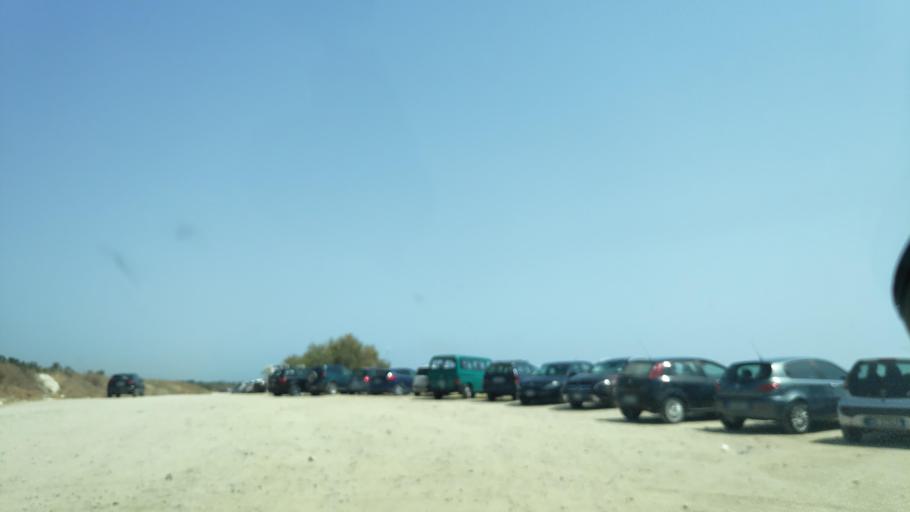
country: IT
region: Calabria
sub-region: Provincia di Catanzaro
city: Guardavalle Marina
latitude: 38.4836
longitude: 16.5803
